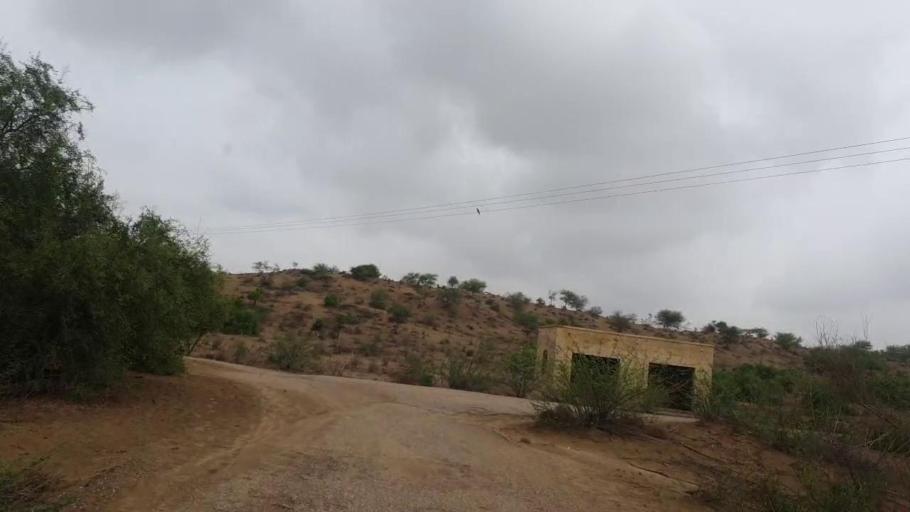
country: PK
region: Sindh
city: Diplo
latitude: 24.5123
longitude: 69.5010
